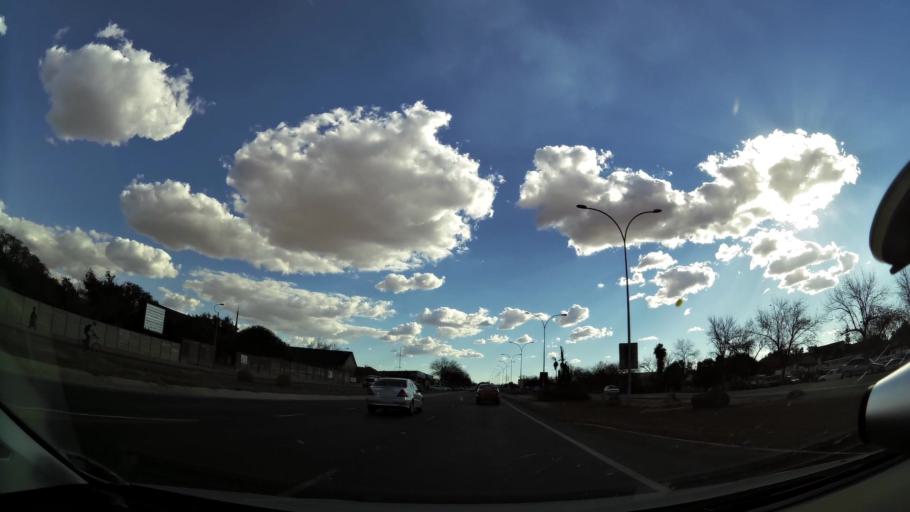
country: ZA
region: North-West
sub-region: Dr Kenneth Kaunda District Municipality
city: Klerksdorp
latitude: -26.8647
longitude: 26.6492
